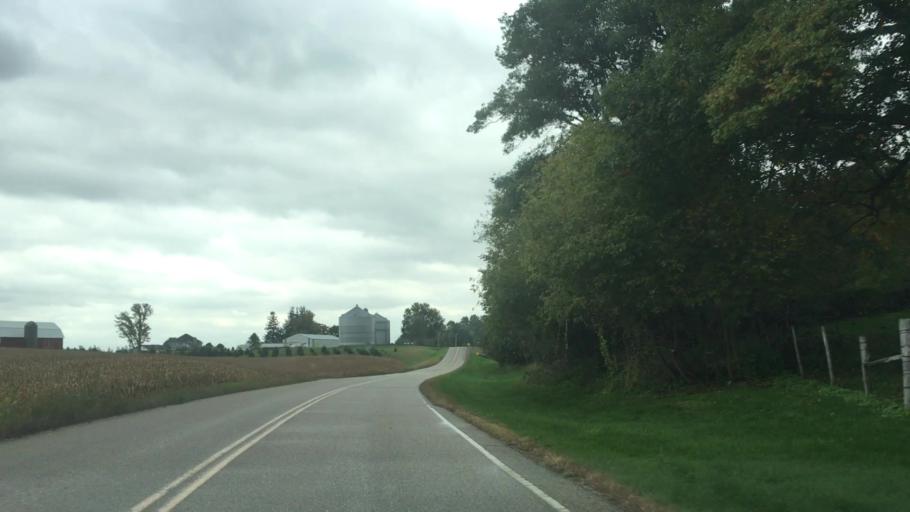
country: US
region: Minnesota
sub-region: Fillmore County
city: Preston
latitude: 43.7375
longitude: -92.0069
